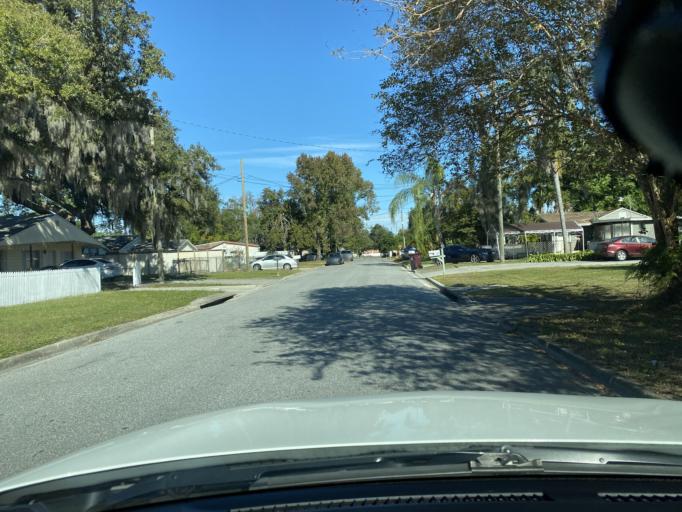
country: US
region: Florida
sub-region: Orange County
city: Conway
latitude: 28.5214
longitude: -81.3156
